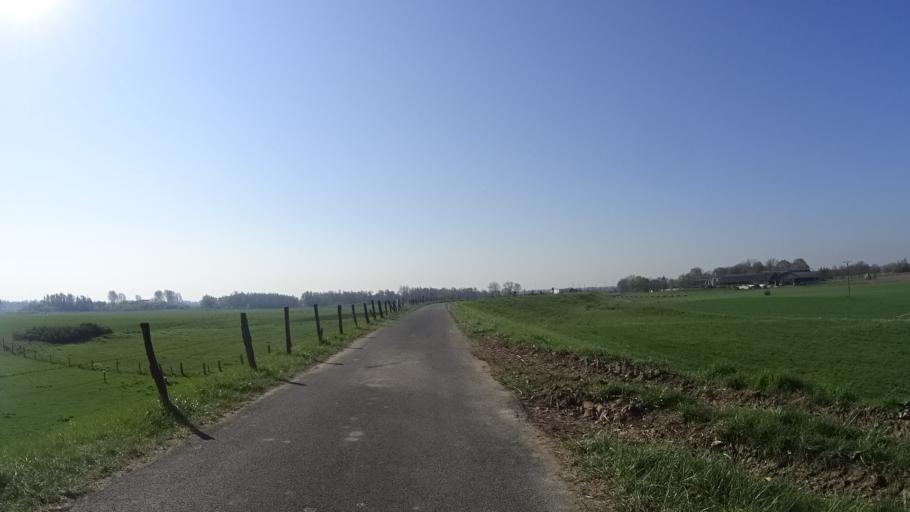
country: DE
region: North Rhine-Westphalia
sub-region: Regierungsbezirk Dusseldorf
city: Alpen
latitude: 51.6143
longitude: 6.5738
